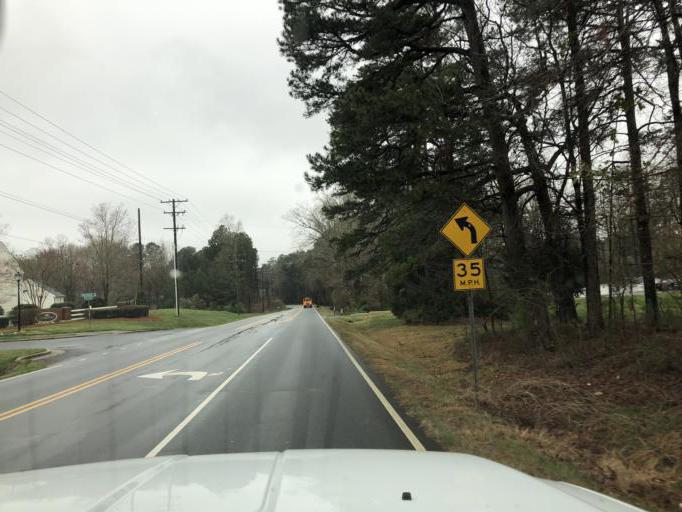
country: US
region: North Carolina
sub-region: Mecklenburg County
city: Huntersville
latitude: 35.3453
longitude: -80.9021
